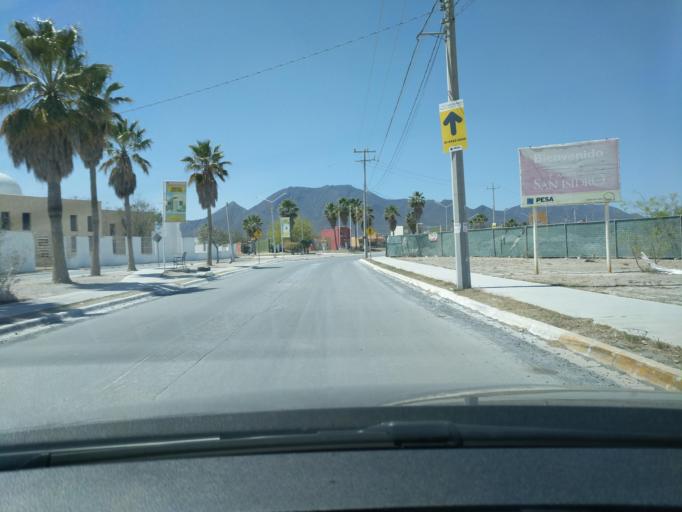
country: MX
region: Nuevo Leon
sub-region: Salinas Victoria
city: Las Torres
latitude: 25.9626
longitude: -100.3038
